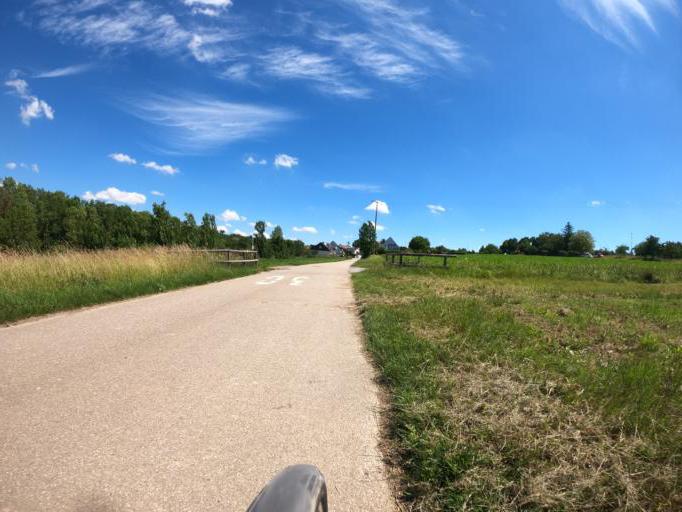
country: DE
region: Baden-Wuerttemberg
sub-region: Regierungsbezirk Stuttgart
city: Bietigheim-Bissingen
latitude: 48.9431
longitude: 9.0866
